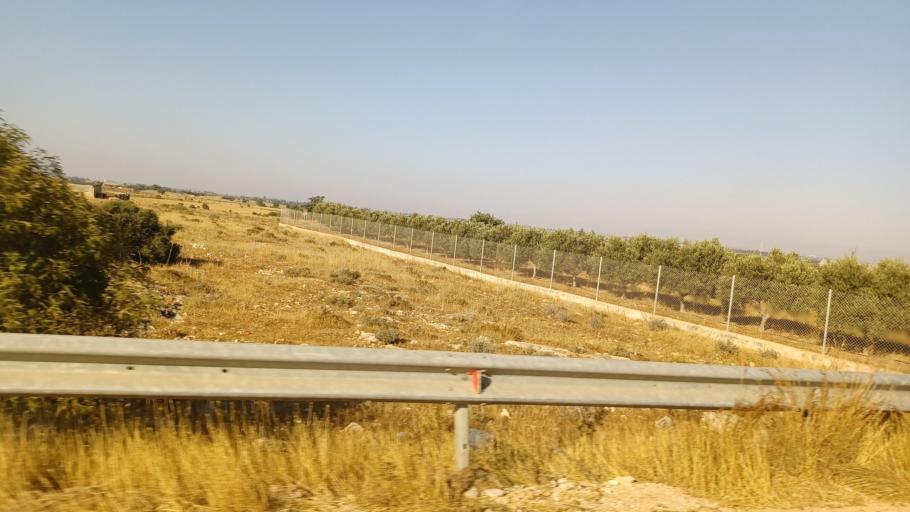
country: CY
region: Ammochostos
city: Frenaros
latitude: 35.0611
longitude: 33.9050
